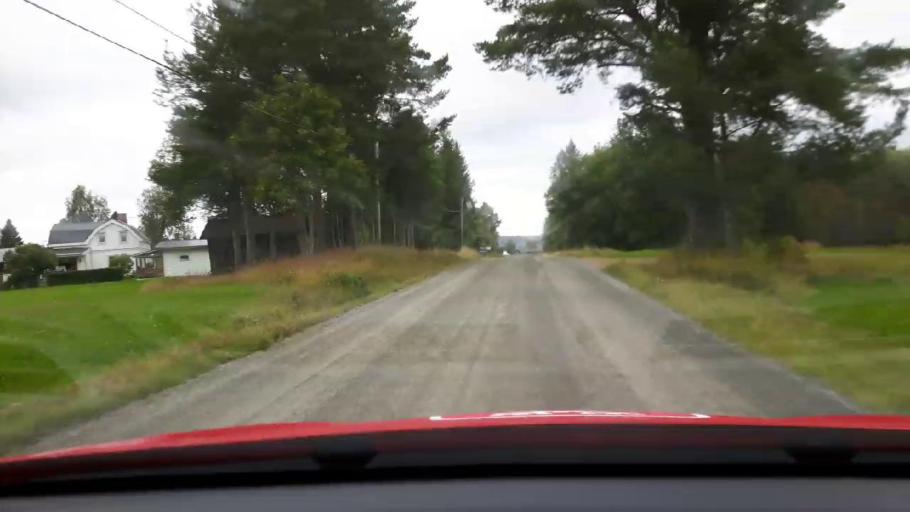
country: SE
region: Jaemtland
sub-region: Bergs Kommun
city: Hoverberg
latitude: 62.8485
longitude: 14.3503
